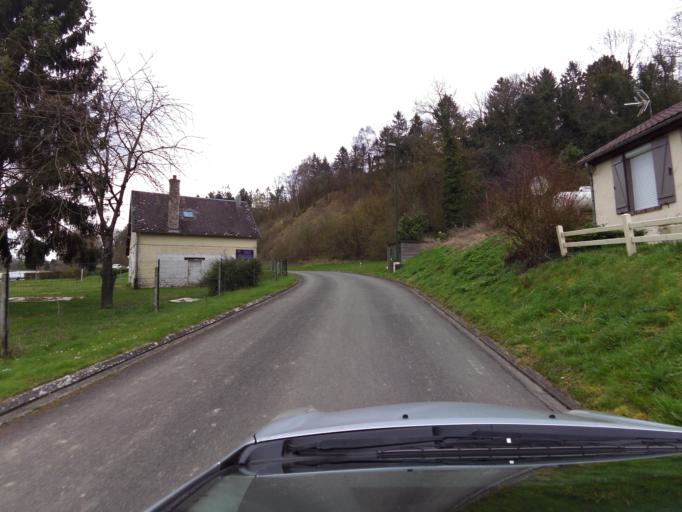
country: FR
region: Picardie
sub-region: Departement de la Somme
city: Bray-sur-Somme
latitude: 49.9333
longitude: 2.8129
